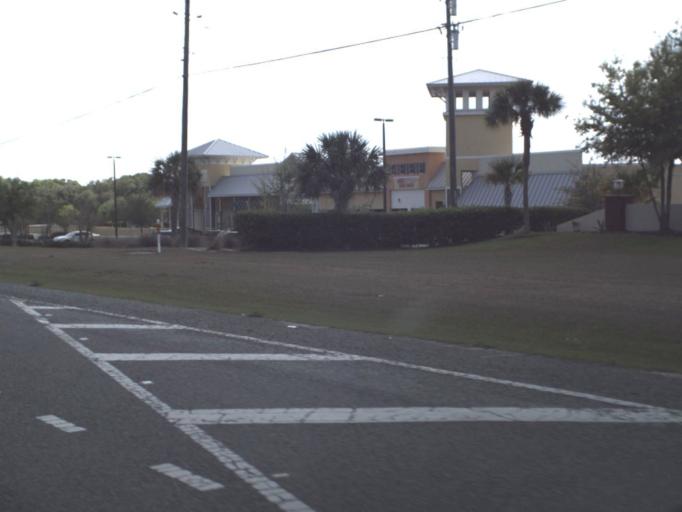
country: US
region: Florida
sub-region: Lake County
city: Hawthorne
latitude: 28.7175
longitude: -81.8615
